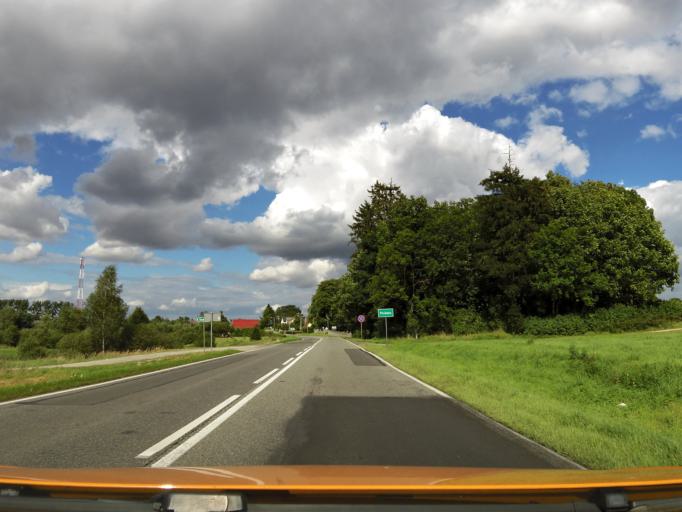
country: PL
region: West Pomeranian Voivodeship
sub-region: Powiat gryficki
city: Brojce
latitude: 53.9000
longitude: 15.4261
